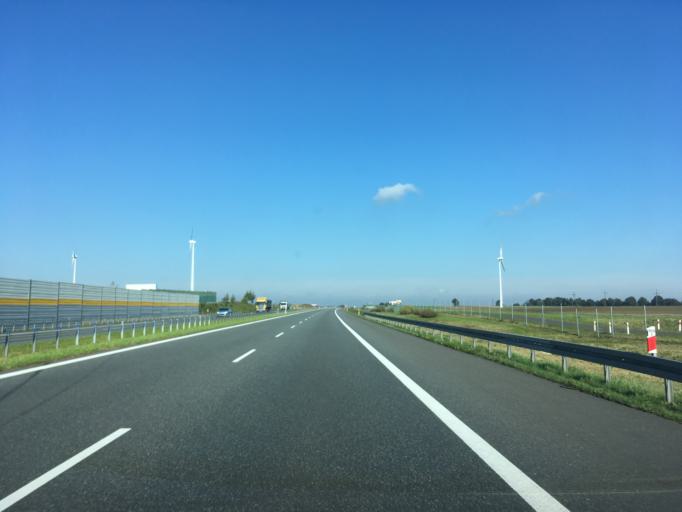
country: PL
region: Kujawsko-Pomorskie
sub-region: Powiat chelminski
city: Lisewo
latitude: 53.3707
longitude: 18.6940
